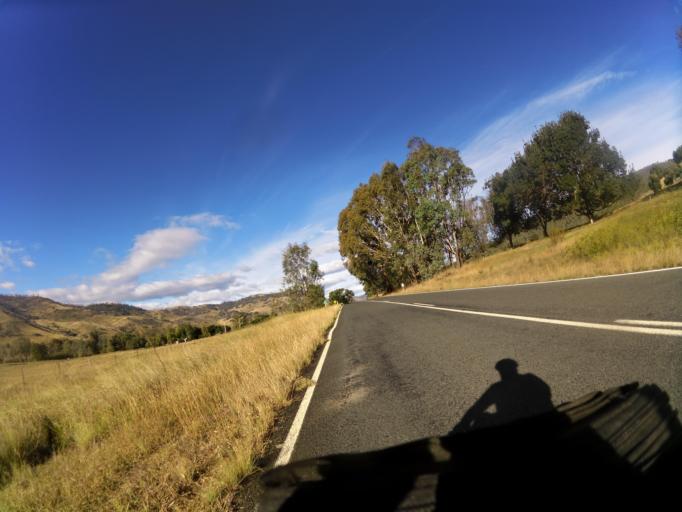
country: AU
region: New South Wales
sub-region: Greater Hume Shire
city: Holbrook
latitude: -35.9707
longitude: 147.7854
